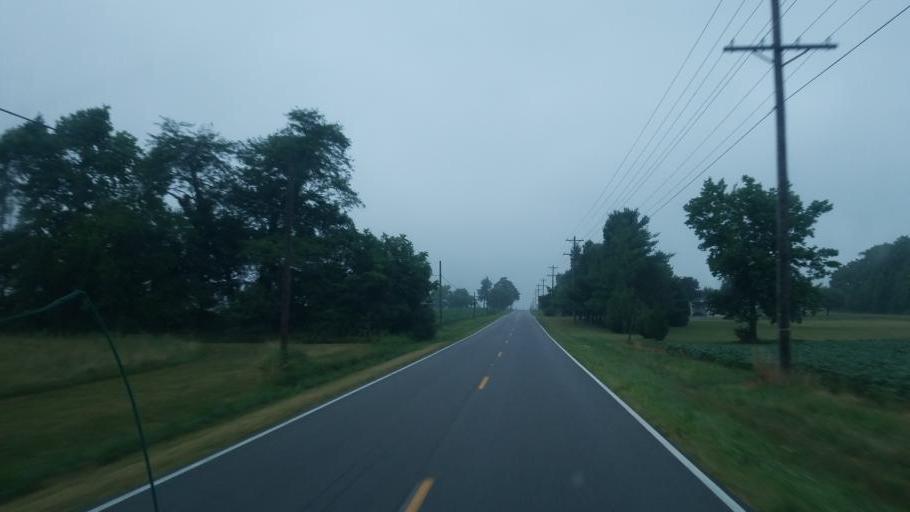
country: US
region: Ohio
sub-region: Defiance County
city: Hicksville
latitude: 41.3462
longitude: -84.7093
